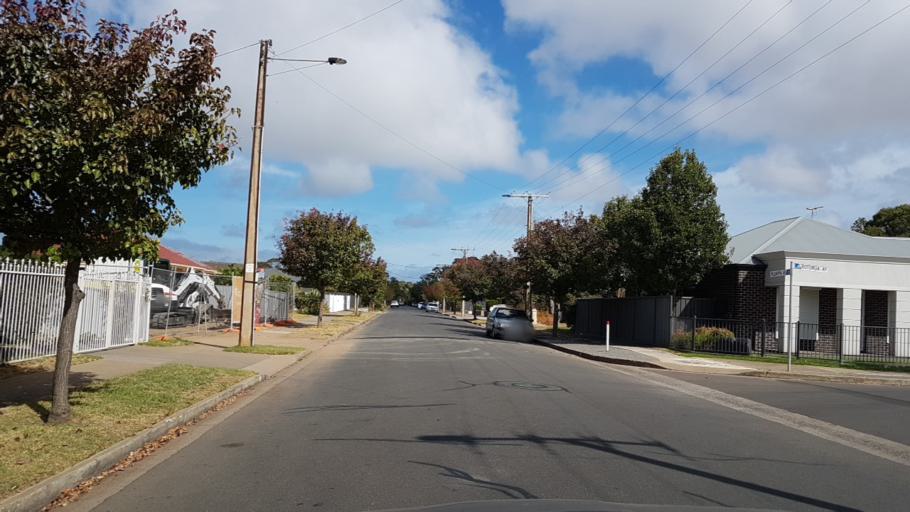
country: AU
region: South Australia
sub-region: Marion
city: Plympton Park
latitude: -34.9903
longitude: 138.5506
